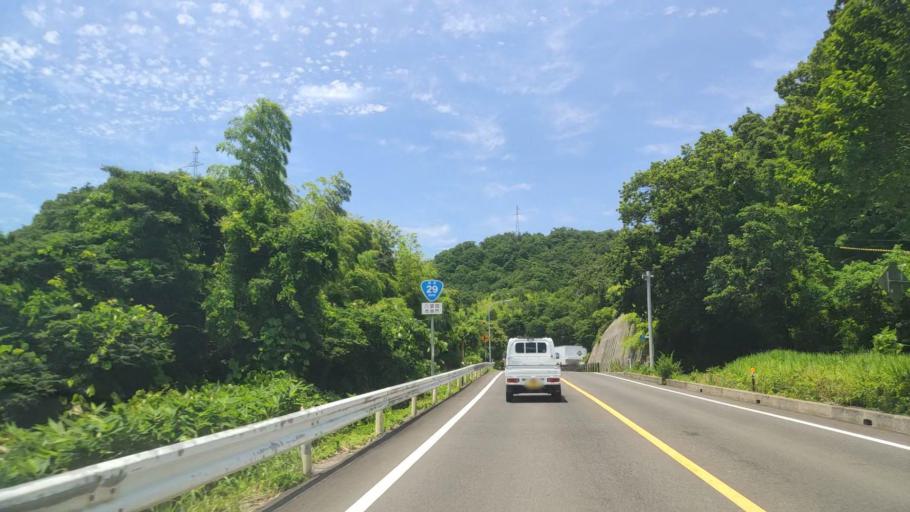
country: JP
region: Tottori
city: Tottori
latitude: 35.3994
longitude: 134.2674
